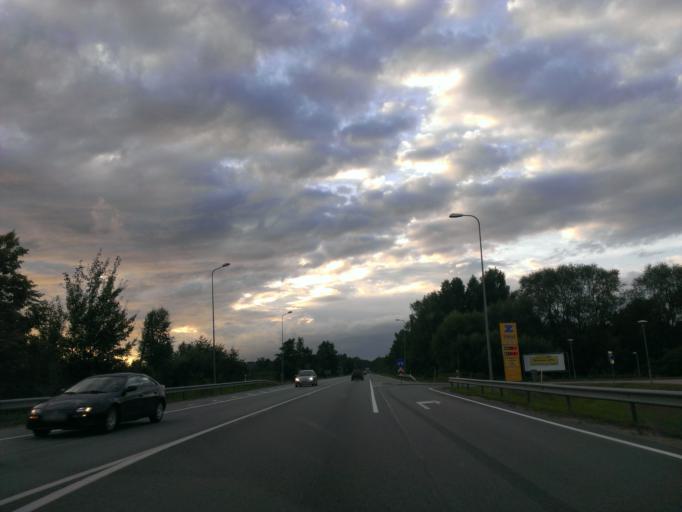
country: LV
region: Riga
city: Bergi
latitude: 56.9735
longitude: 24.3412
